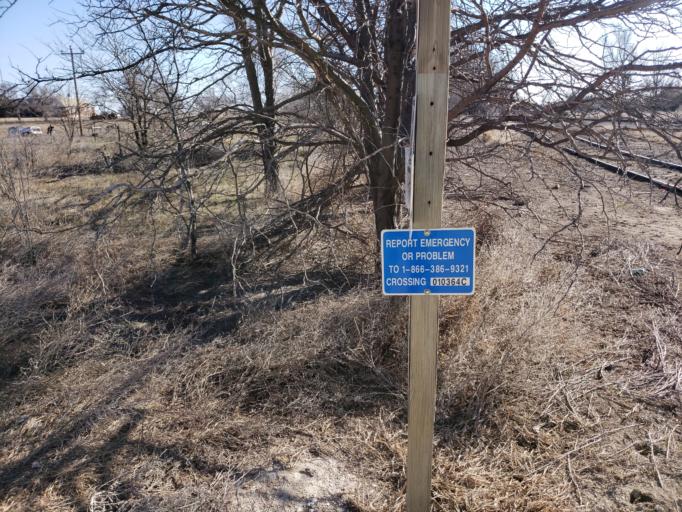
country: US
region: Kansas
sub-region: Lane County
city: Dighton
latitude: 38.4436
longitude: -100.1945
